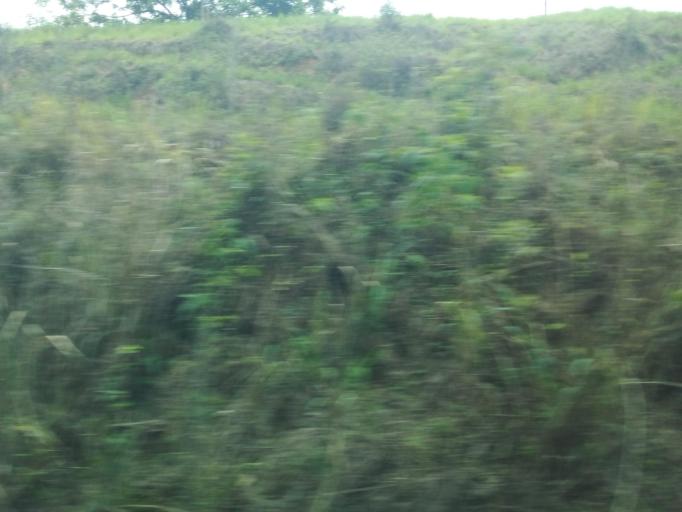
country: BR
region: Minas Gerais
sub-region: Ipaba
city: Ipaba
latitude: -19.4625
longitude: -42.4678
